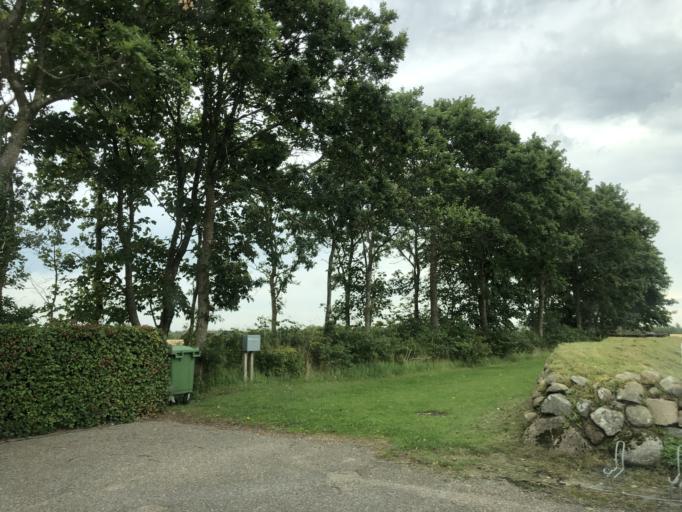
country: DK
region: Central Jutland
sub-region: Holstebro Kommune
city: Ulfborg
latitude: 56.3621
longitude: 8.4448
